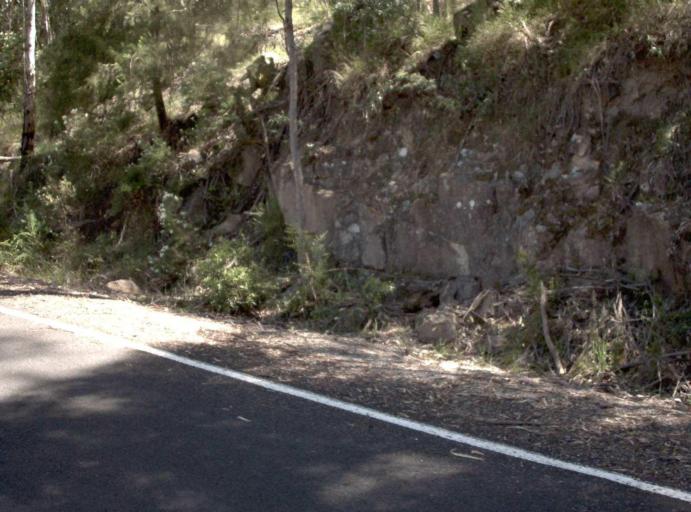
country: AU
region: Victoria
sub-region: East Gippsland
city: Lakes Entrance
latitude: -37.3797
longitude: 148.2189
